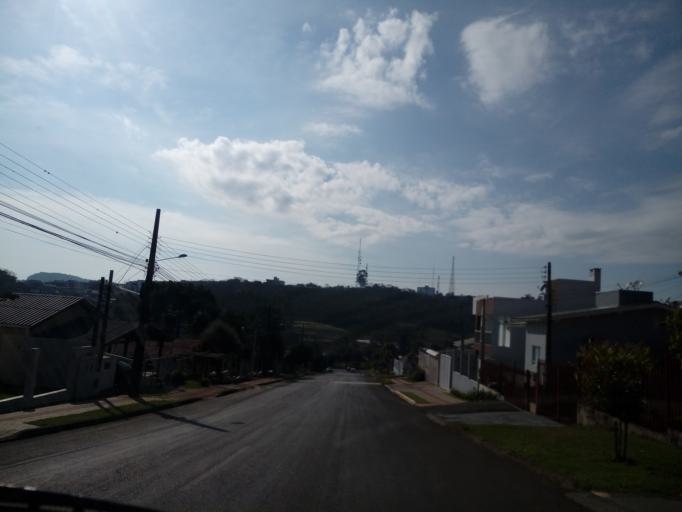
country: BR
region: Santa Catarina
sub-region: Chapeco
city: Chapeco
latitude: -27.1082
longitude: -52.5924
